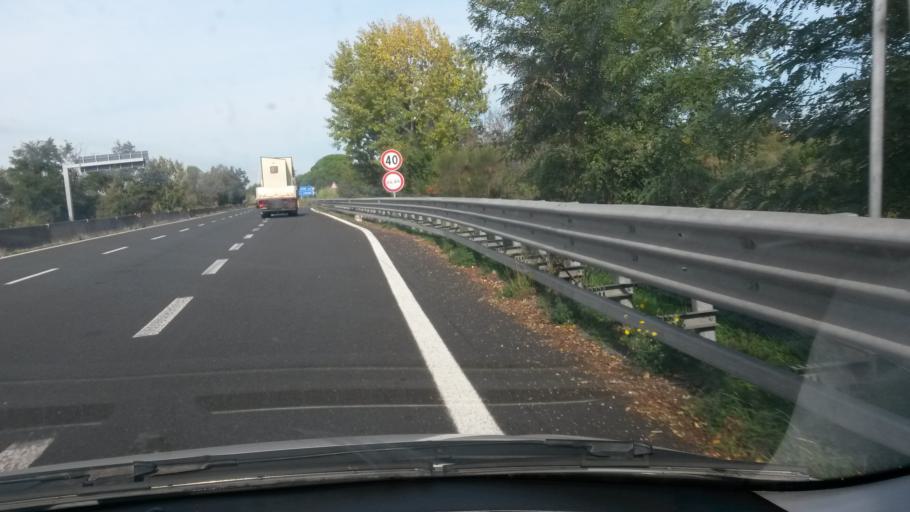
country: IT
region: Tuscany
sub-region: Provincia di Livorno
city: S.P. in Palazzi
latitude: 43.3325
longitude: 10.5260
